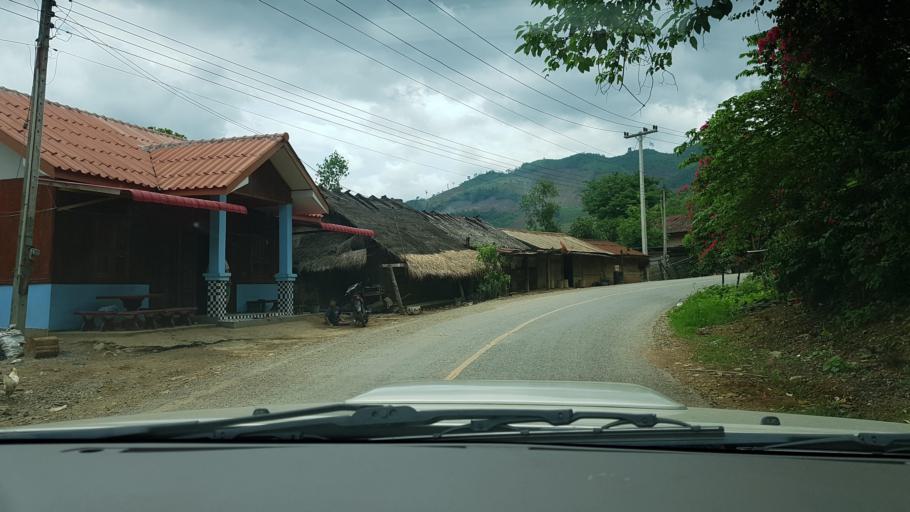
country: TH
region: Nan
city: Chaloem Phra Kiat
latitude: 19.9636
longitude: 101.2634
